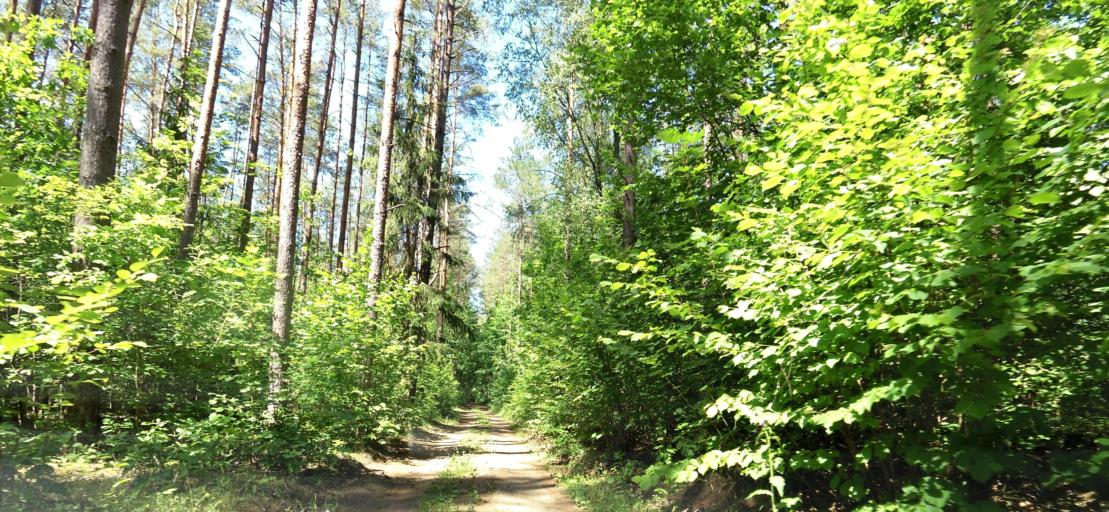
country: LT
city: Grigiskes
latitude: 54.7880
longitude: 24.9672
